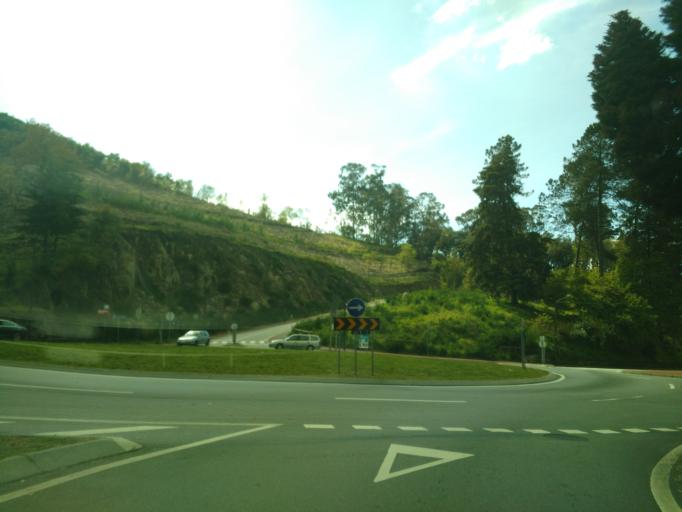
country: PT
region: Braga
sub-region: Braga
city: Braga
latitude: 41.5401
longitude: -8.4114
